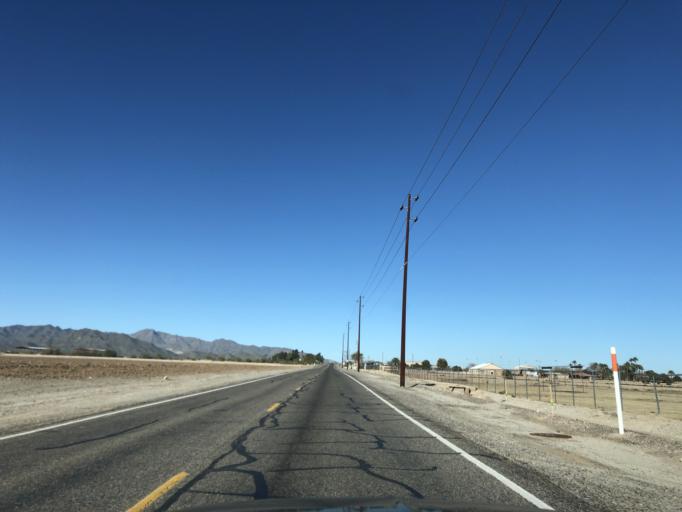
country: US
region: Arizona
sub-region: Maricopa County
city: Buckeye
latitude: 33.4252
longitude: -112.5042
